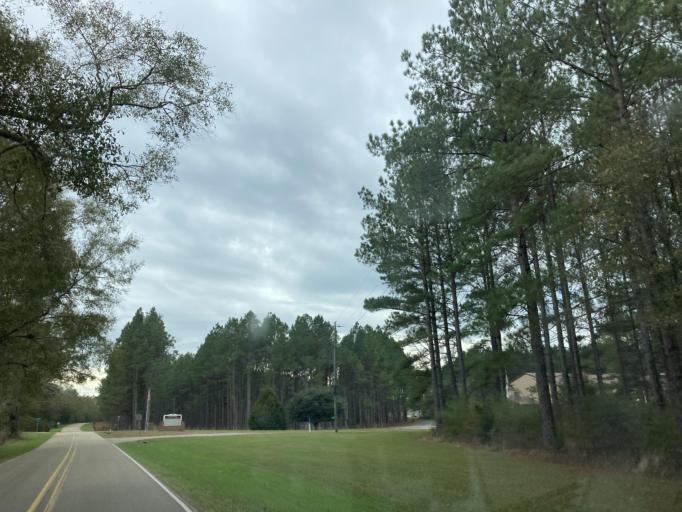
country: US
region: Mississippi
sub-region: Stone County
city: Wiggins
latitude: 30.9631
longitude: -89.2682
